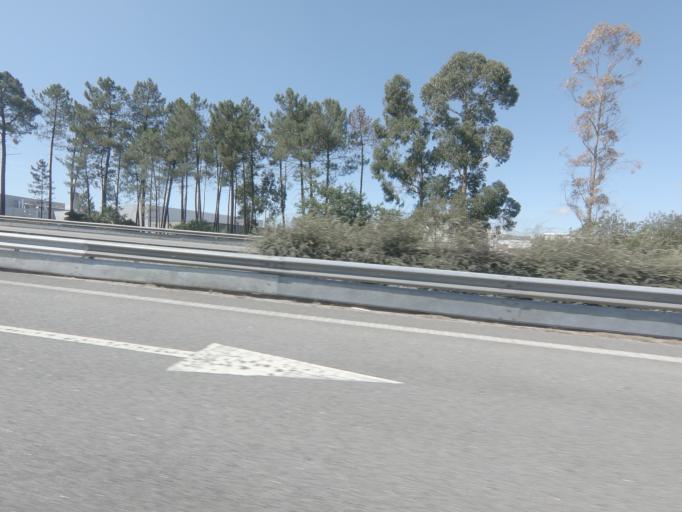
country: PT
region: Porto
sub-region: Paredes
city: Gandra
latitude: 41.1755
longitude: -8.4399
